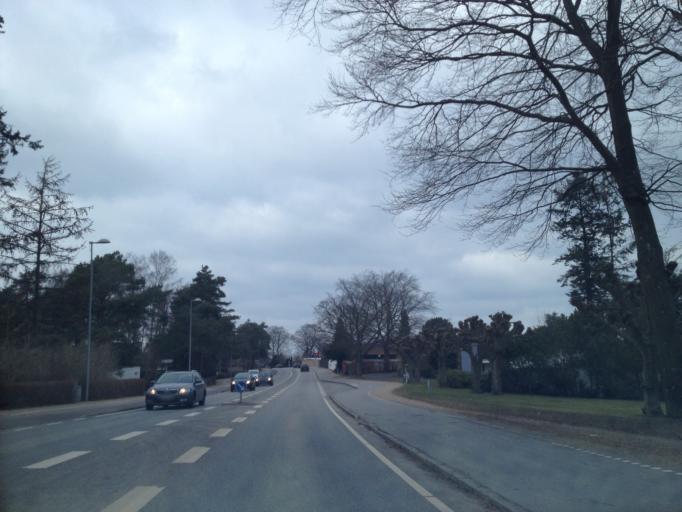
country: DK
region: Capital Region
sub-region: Rudersdal Kommune
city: Trorod
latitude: 55.8710
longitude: 12.5502
